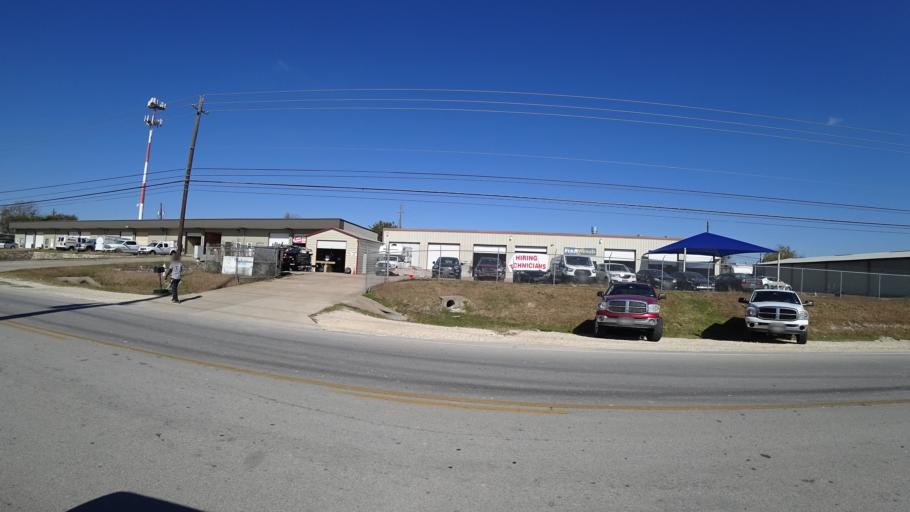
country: US
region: Texas
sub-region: Travis County
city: Wells Branch
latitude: 30.4299
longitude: -97.6829
